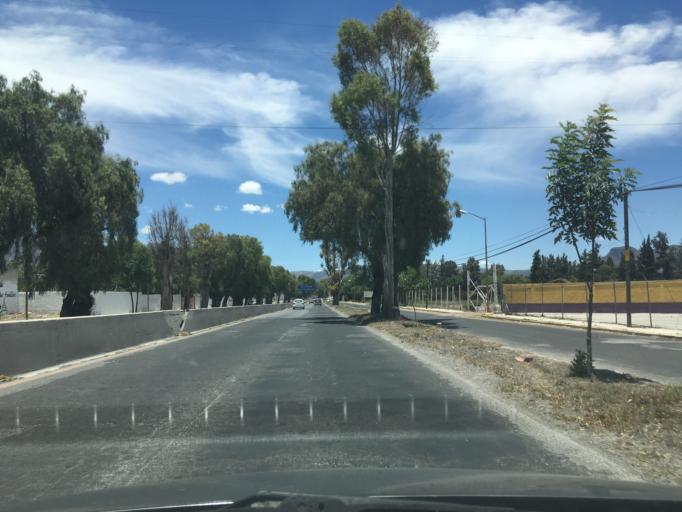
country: MX
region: Hidalgo
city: Actopan
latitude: 20.2581
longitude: -98.9396
